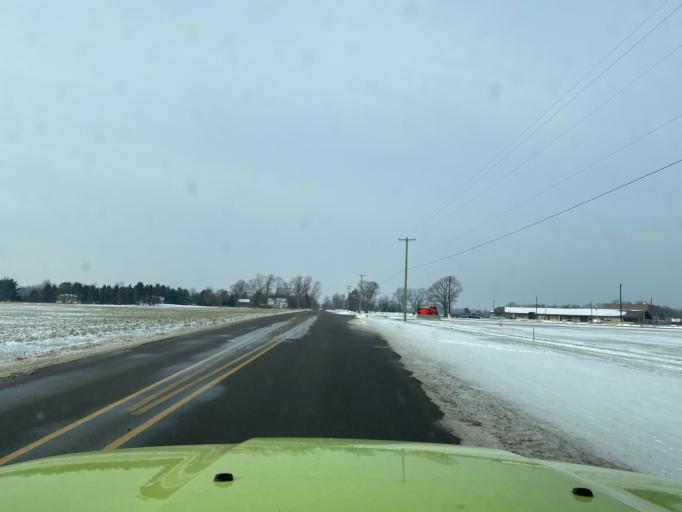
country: US
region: Michigan
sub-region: Ottawa County
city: Allendale
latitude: 42.9577
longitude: -85.9604
